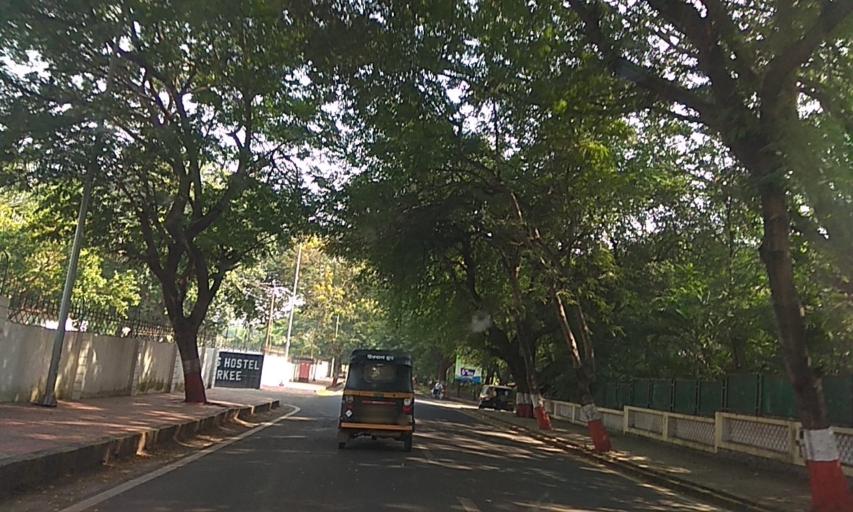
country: IN
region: Maharashtra
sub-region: Pune Division
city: Khadki
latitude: 18.5590
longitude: 73.8520
